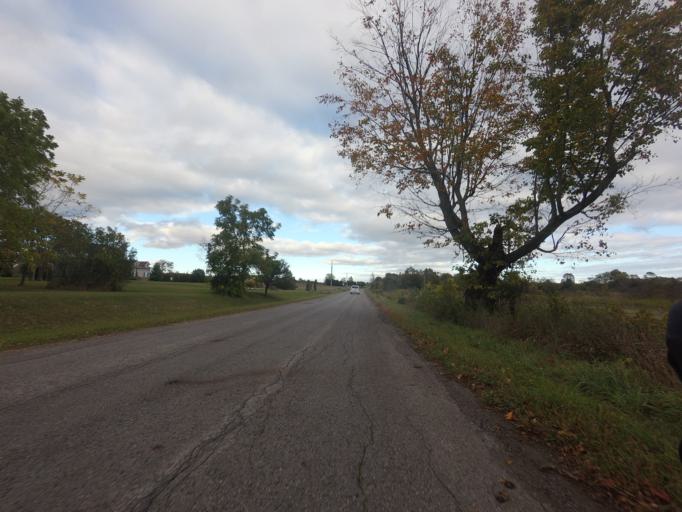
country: CA
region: Ontario
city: Cobourg
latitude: 43.9778
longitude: -77.9438
